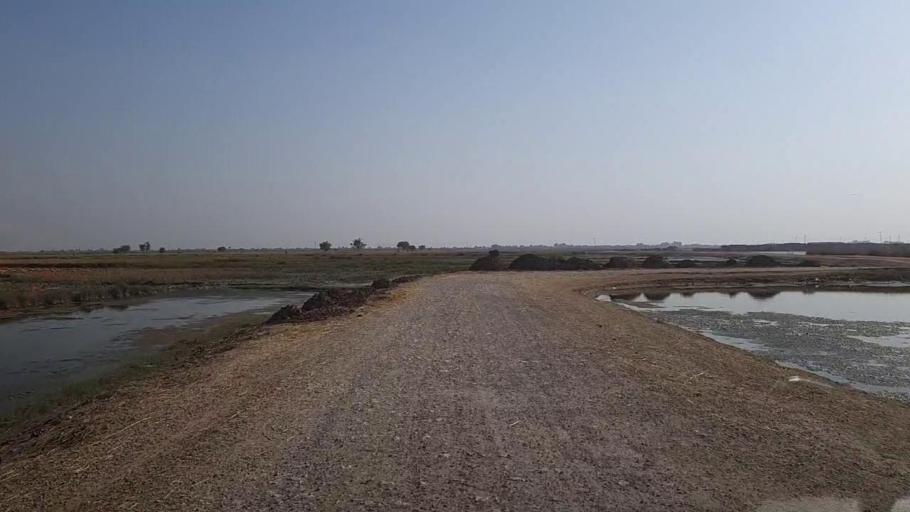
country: PK
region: Sindh
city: Kandhkot
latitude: 28.3730
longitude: 69.3333
